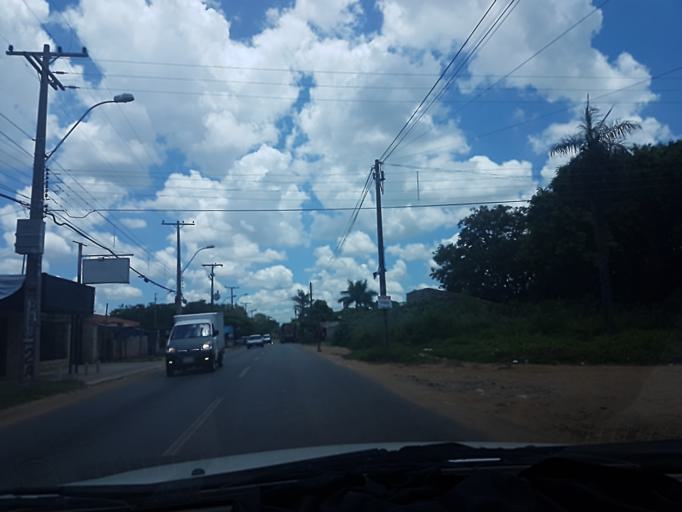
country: PY
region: Central
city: Colonia Mariano Roque Alonso
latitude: -25.2056
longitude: -57.5193
